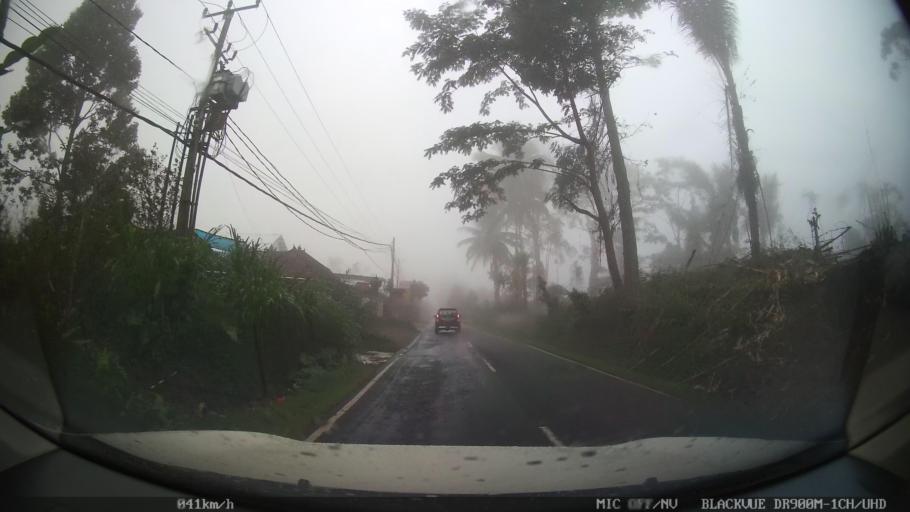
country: ID
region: Bali
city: Banjar Taro Kelod
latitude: -8.3382
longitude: 115.2828
